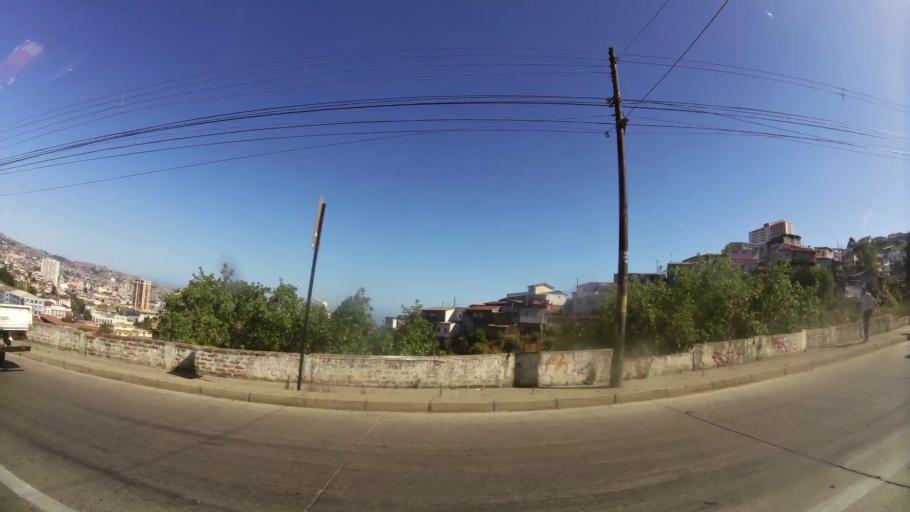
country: CL
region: Valparaiso
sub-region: Provincia de Valparaiso
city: Valparaiso
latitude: -33.0531
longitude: -71.5983
